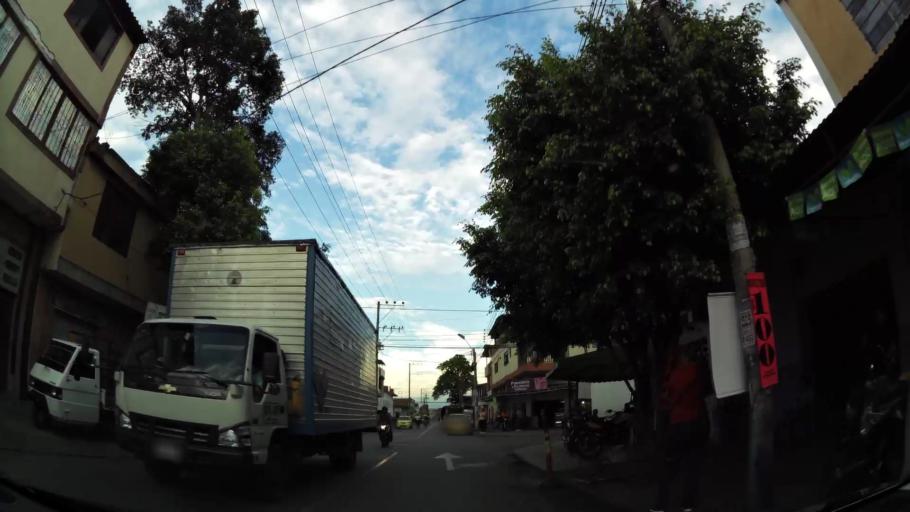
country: CO
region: Valle del Cauca
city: Cali
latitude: 3.4602
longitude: -76.5154
